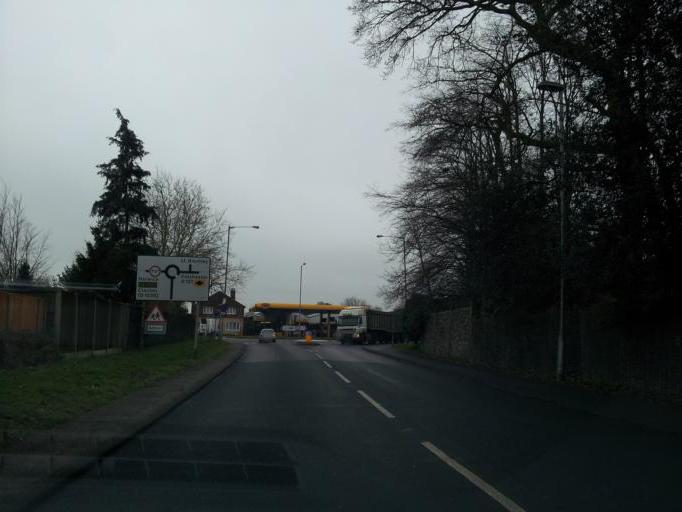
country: GB
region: England
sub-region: Essex
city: Manningtree
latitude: 51.9393
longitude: 1.0455
